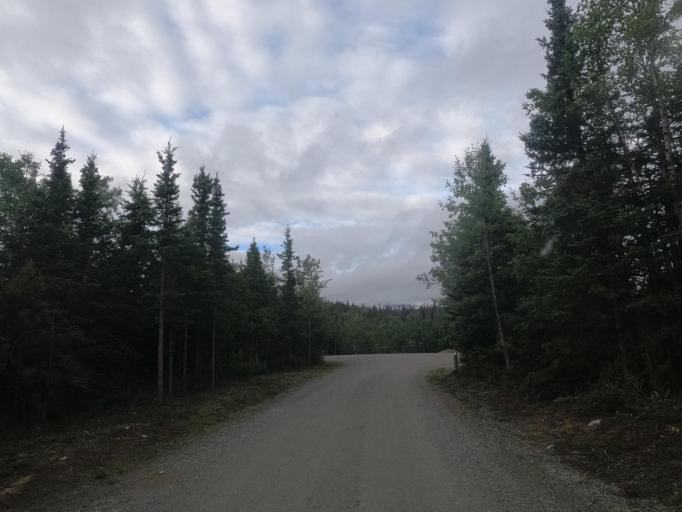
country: CA
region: Yukon
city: Haines Junction
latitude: 60.1076
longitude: -136.9457
